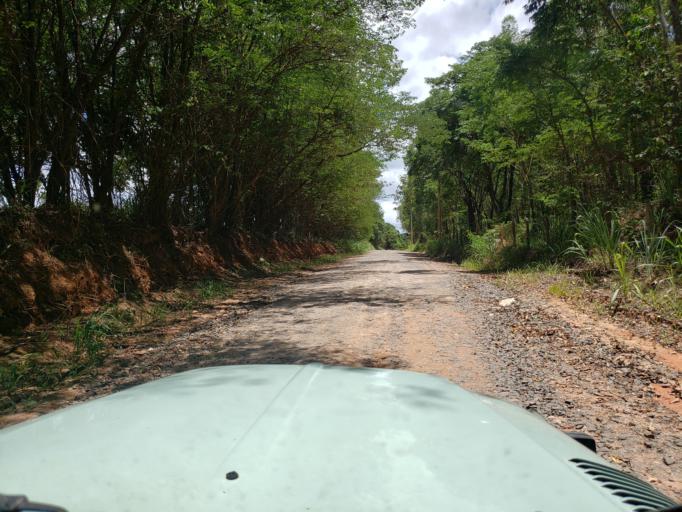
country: BR
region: Sao Paulo
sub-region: Moji-Guacu
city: Mogi-Gaucu
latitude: -22.2553
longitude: -46.8490
